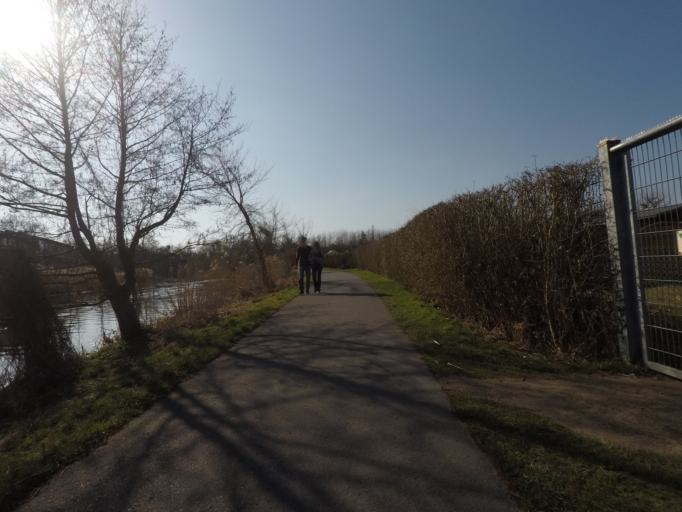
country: DE
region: Brandenburg
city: Eberswalde
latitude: 52.8390
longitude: 13.8042
